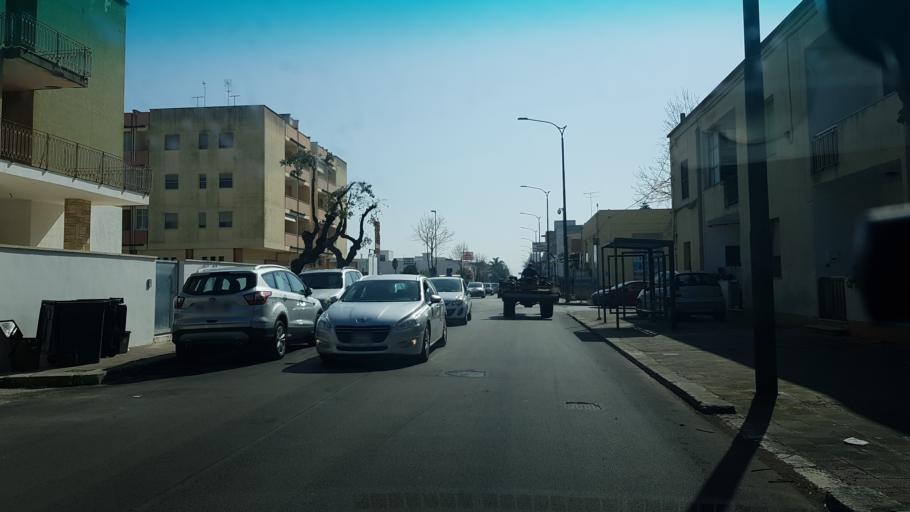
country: IT
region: Apulia
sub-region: Provincia di Brindisi
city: San Pietro Vernotico
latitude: 40.4828
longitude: 18.0033
